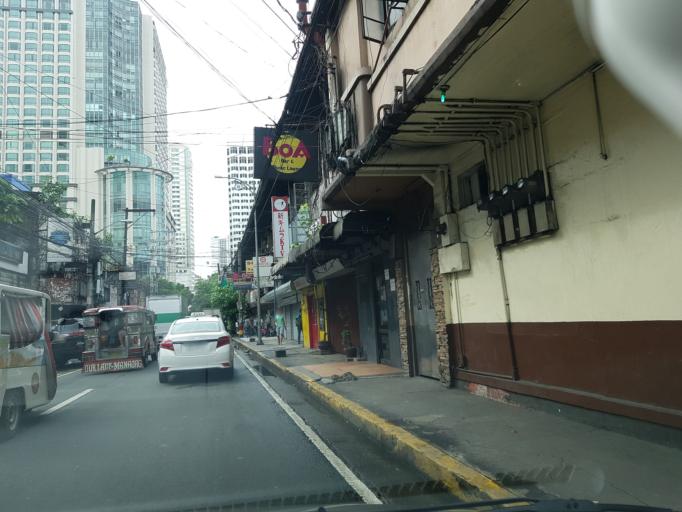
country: PH
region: Metro Manila
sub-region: City of Manila
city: Port Area
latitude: 14.5748
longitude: 120.9815
